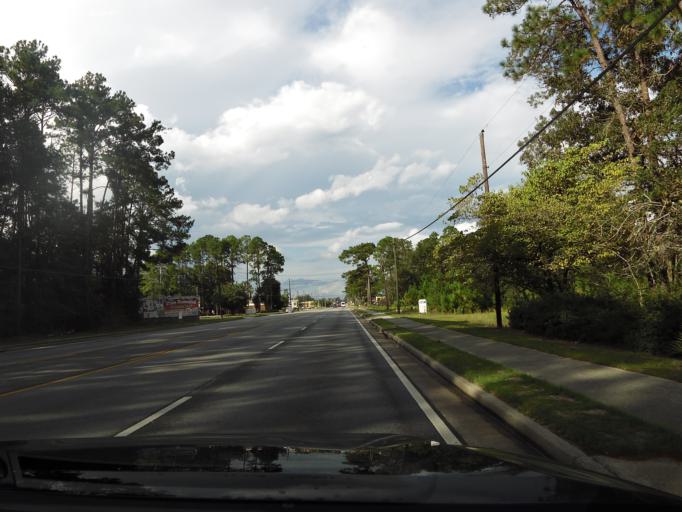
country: US
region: Georgia
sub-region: Liberty County
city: Hinesville
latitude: 31.8177
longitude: -81.6008
